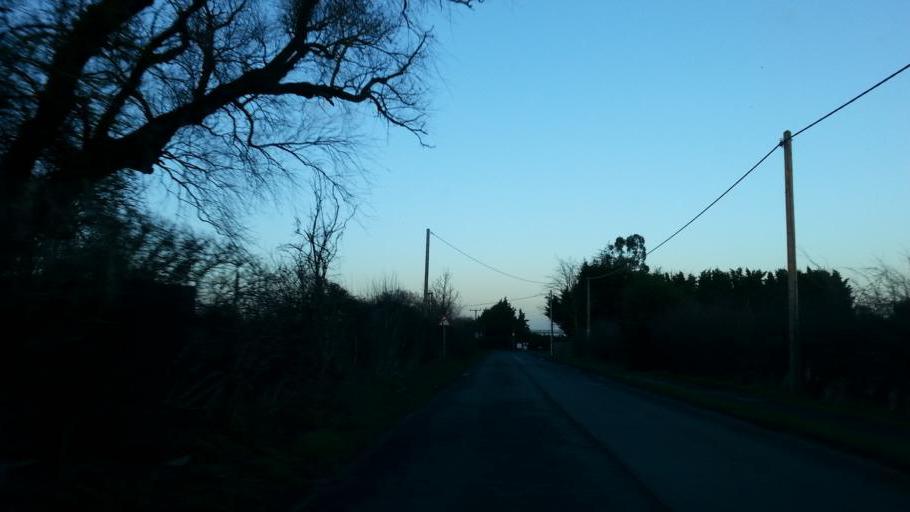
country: GB
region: England
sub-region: Cambridgeshire
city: Needingworth
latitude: 52.2981
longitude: -0.0501
